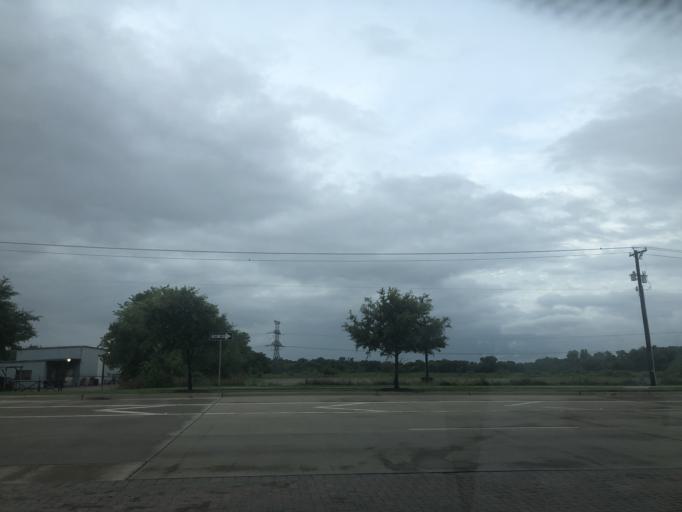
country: US
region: Texas
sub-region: Dallas County
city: Irving
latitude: 32.7832
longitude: -96.9688
